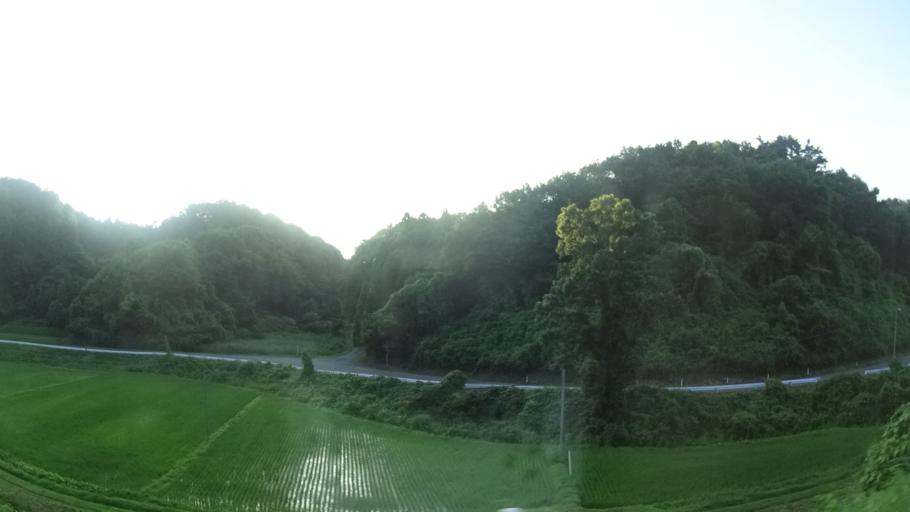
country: JP
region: Fukushima
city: Miharu
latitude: 37.4635
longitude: 140.5252
